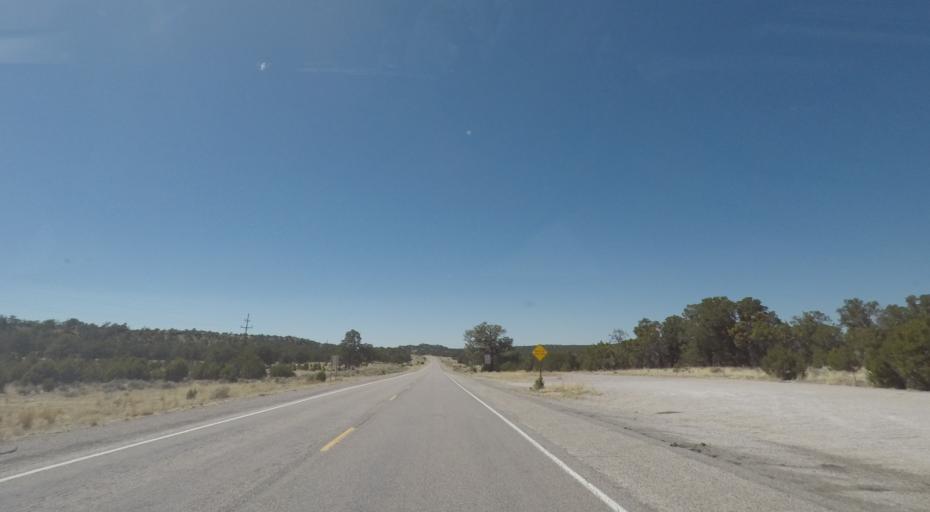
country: US
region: New Mexico
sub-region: Socorro County
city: Alamo
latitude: 34.3024
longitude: -108.1403
